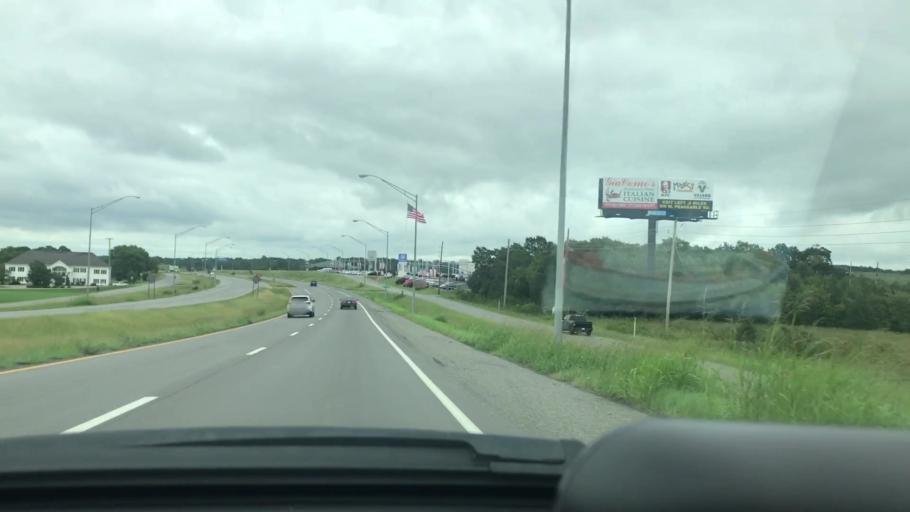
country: US
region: Oklahoma
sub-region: Pittsburg County
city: McAlester
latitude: 34.8987
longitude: -95.7564
